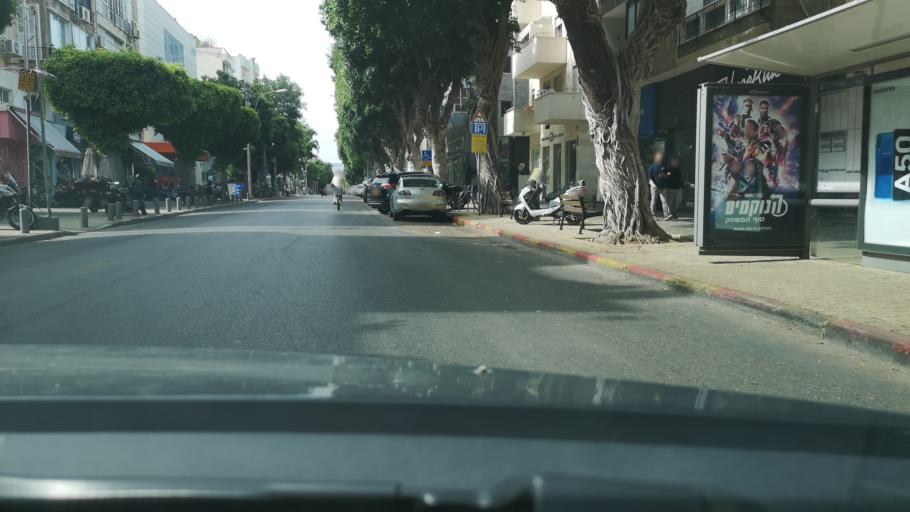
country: IL
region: Tel Aviv
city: Tel Aviv
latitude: 32.0916
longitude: 34.7761
